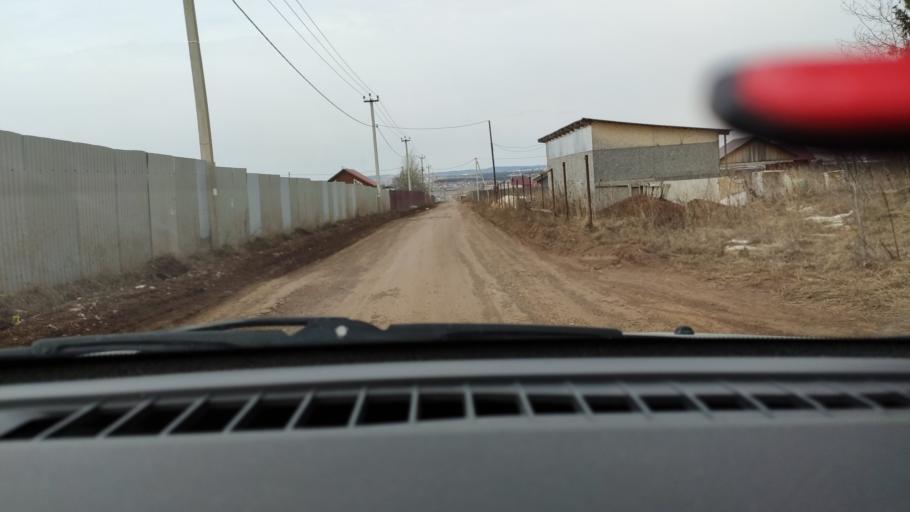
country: RU
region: Perm
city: Kultayevo
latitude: 57.8982
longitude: 56.0106
